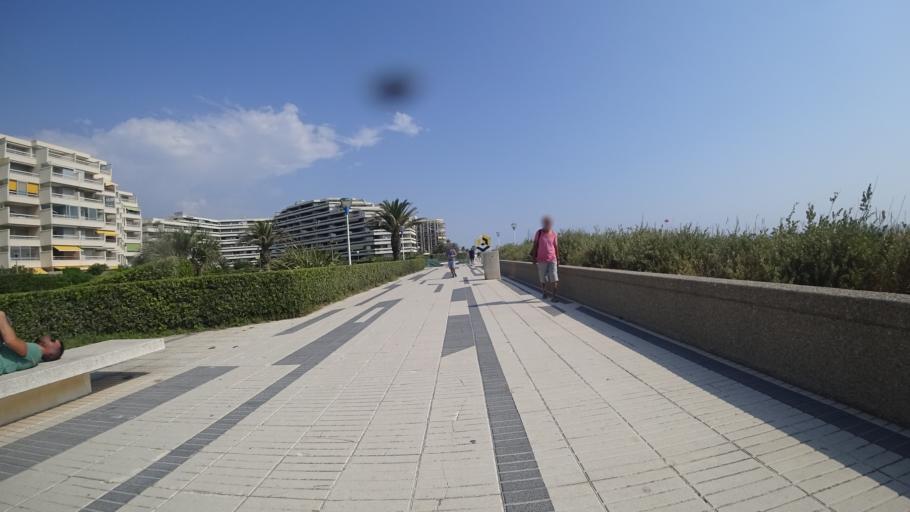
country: FR
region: Languedoc-Roussillon
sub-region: Departement des Pyrenees-Orientales
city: Canet-en-Roussillon
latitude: 42.6772
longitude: 3.0339
